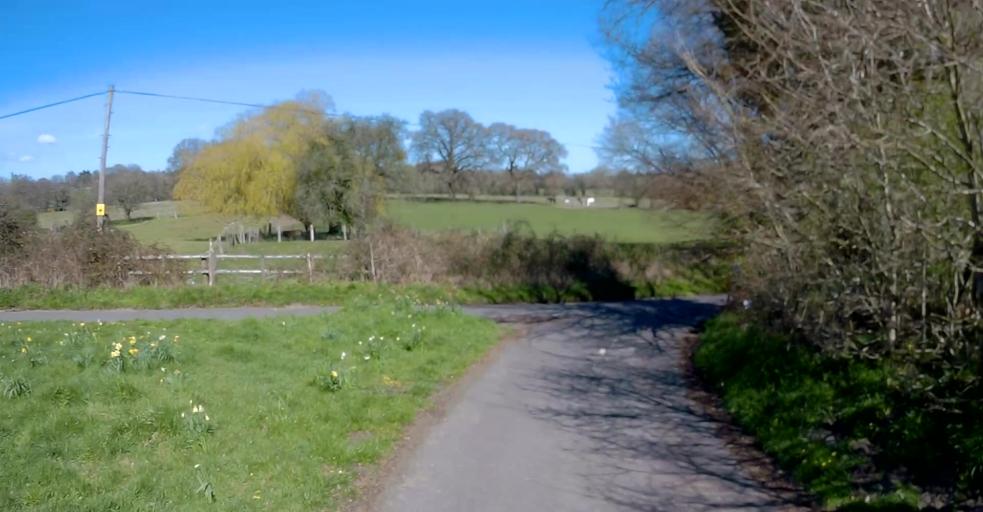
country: GB
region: England
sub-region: Surrey
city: Farnham
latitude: 51.1731
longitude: -0.8096
